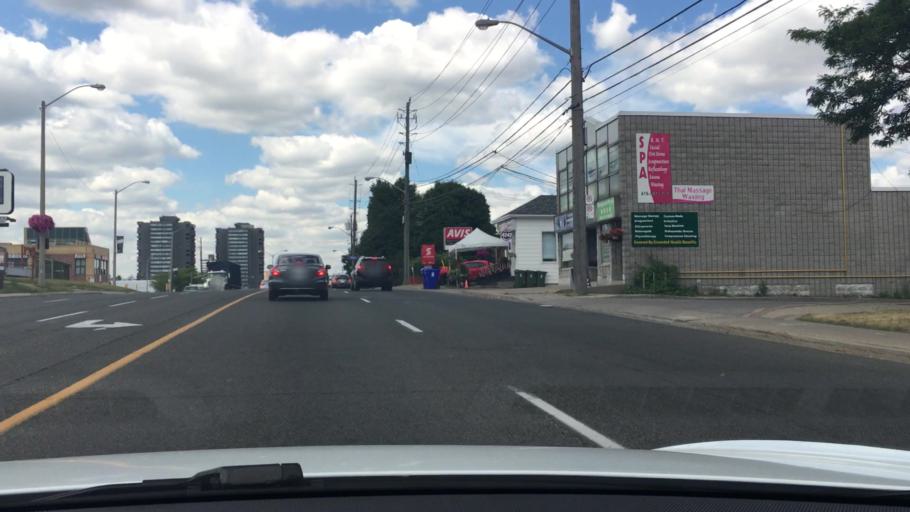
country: CA
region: Ontario
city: Scarborough
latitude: 43.7859
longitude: -79.2765
